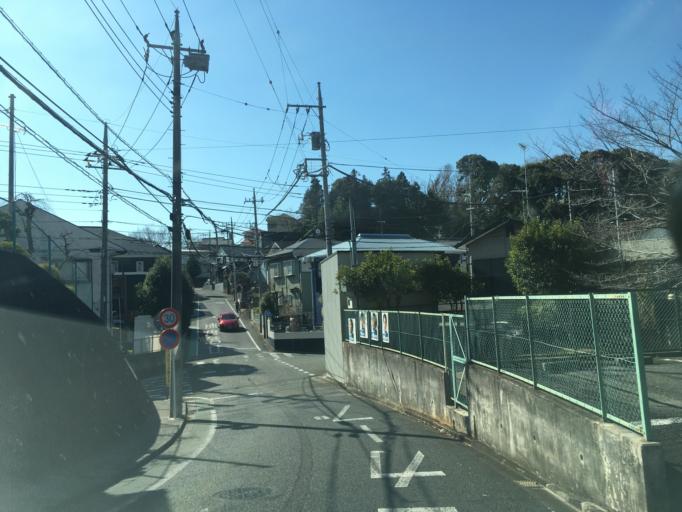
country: JP
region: Tokyo
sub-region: Machida-shi
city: Machida
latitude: 35.5827
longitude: 139.4171
